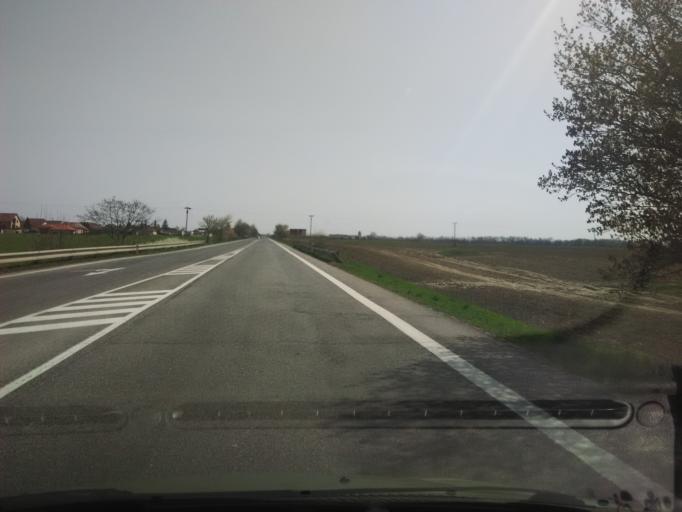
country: SK
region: Nitriansky
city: Sellye
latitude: 48.1707
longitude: 17.8314
